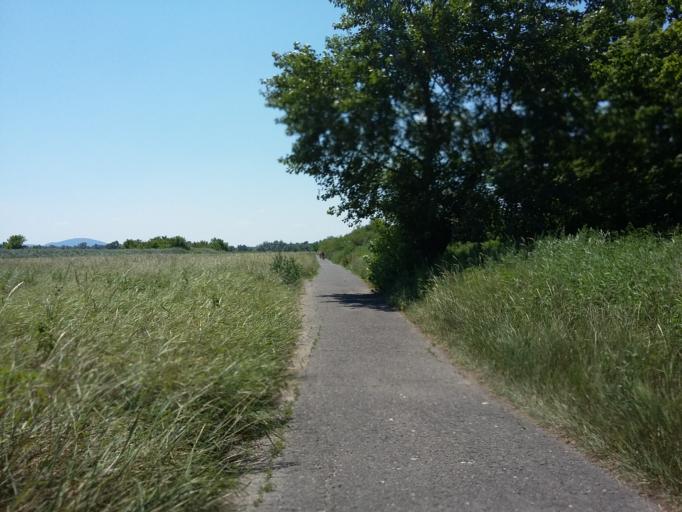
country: AT
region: Lower Austria
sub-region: Politischer Bezirk Ganserndorf
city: Marchegg
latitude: 48.2594
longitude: 16.9554
